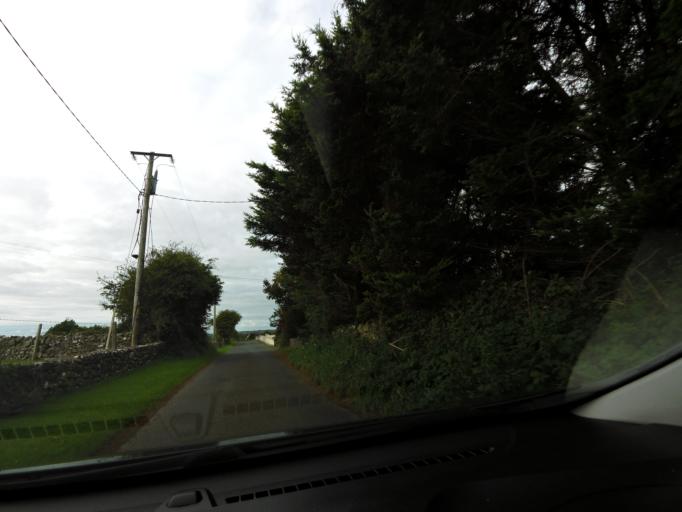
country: IE
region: Connaught
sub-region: County Galway
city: Ballinasloe
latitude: 53.3846
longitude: -8.1787
